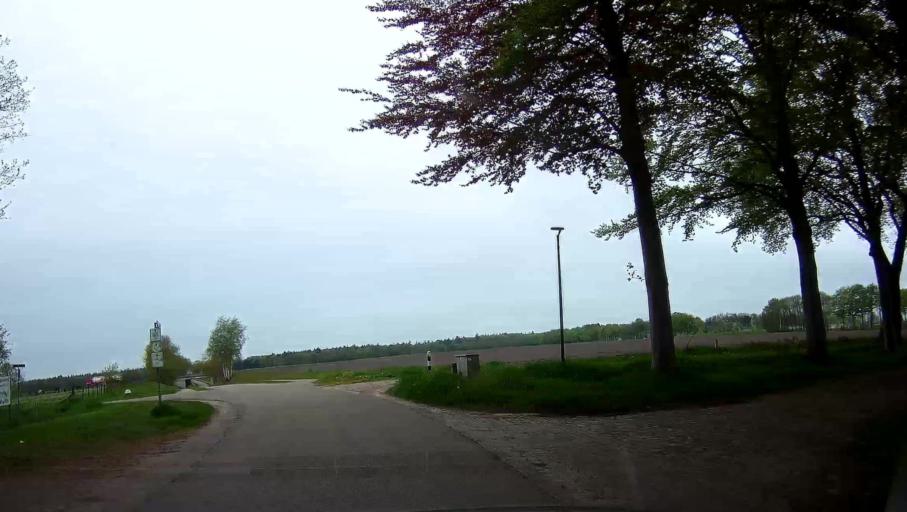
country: NL
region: Drenthe
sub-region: Gemeente Borger-Odoorn
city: Borger
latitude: 52.9721
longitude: 6.7811
